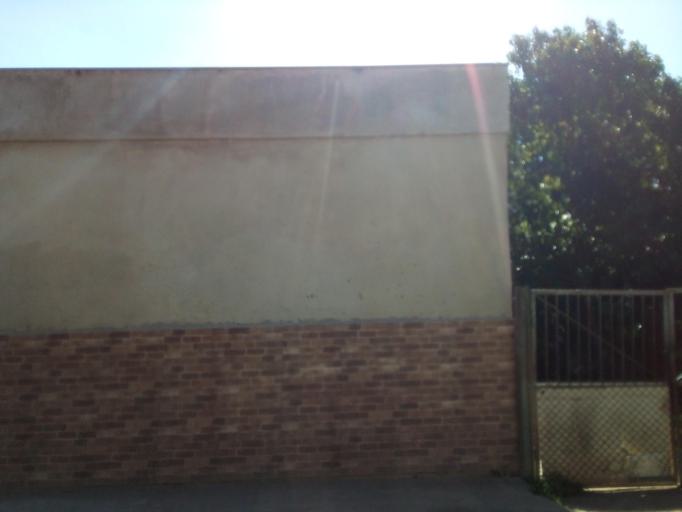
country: BR
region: Espirito Santo
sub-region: Vitoria
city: Vitoria
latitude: -20.2849
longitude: -40.3762
